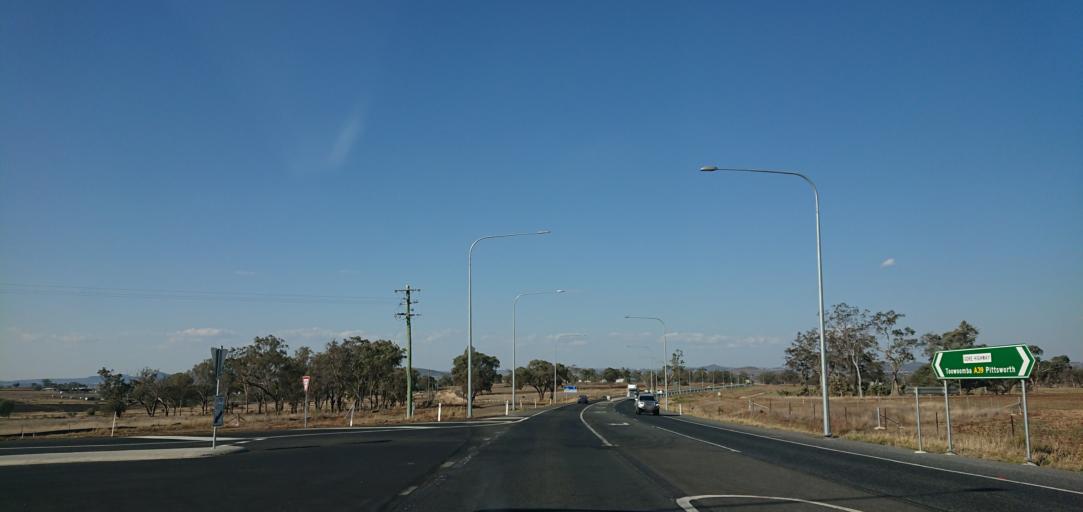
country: AU
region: Queensland
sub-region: Toowoomba
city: Westbrook
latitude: -27.6208
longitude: 151.7667
